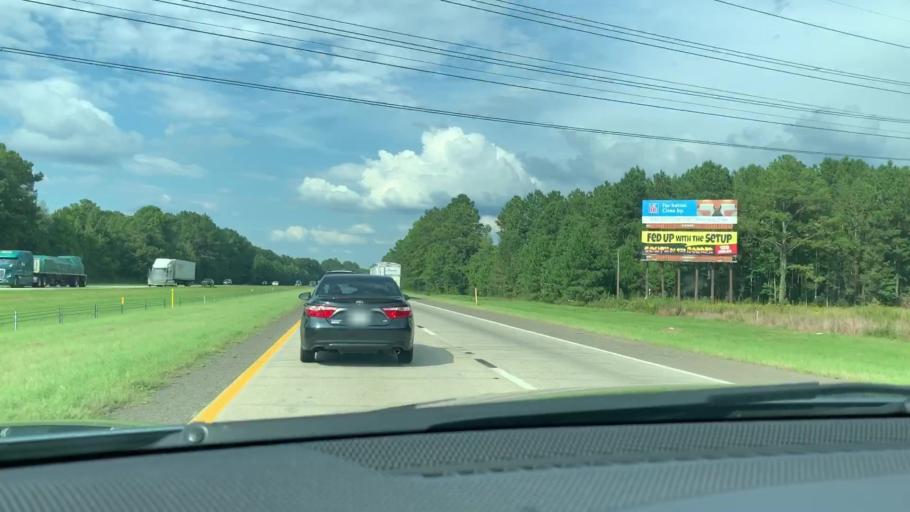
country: US
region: South Carolina
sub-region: Hampton County
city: Yemassee
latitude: 32.6844
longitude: -80.8813
